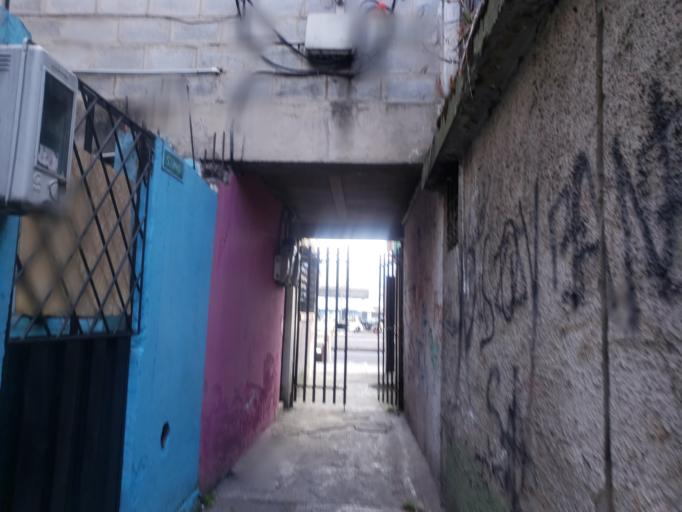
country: EC
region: Pichincha
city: Quito
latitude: -0.2690
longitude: -78.5454
